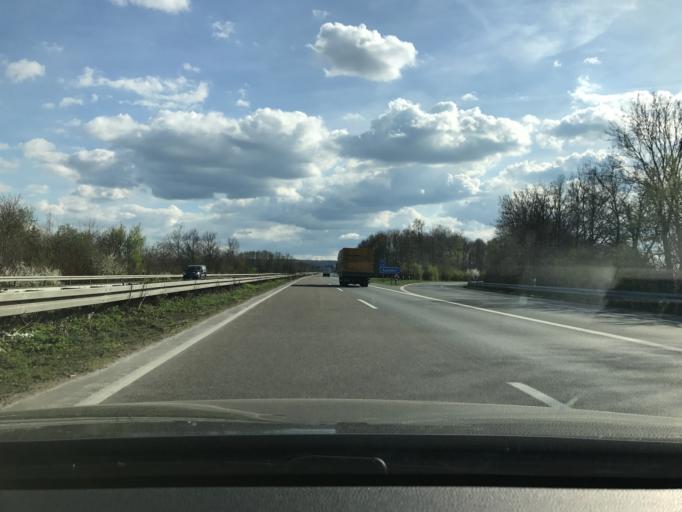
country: DE
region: North Rhine-Westphalia
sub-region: Regierungsbezirk Arnsberg
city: Werl
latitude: 51.5506
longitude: 7.8913
